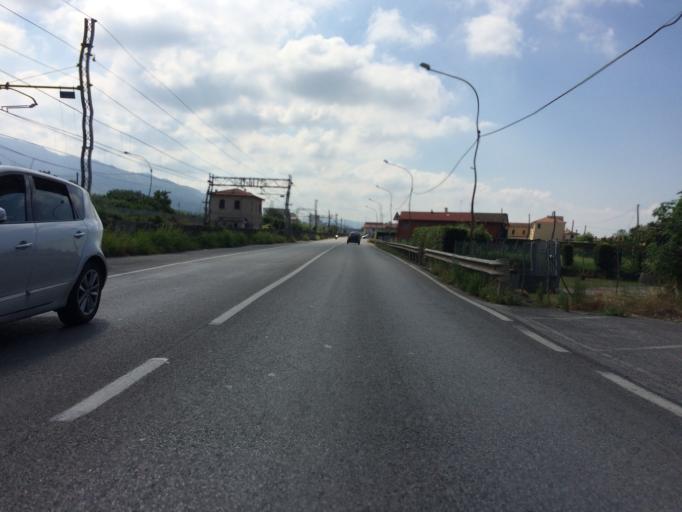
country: IT
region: Tuscany
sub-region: Provincia di Lucca
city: Strettoia
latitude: 43.9852
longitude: 10.1890
